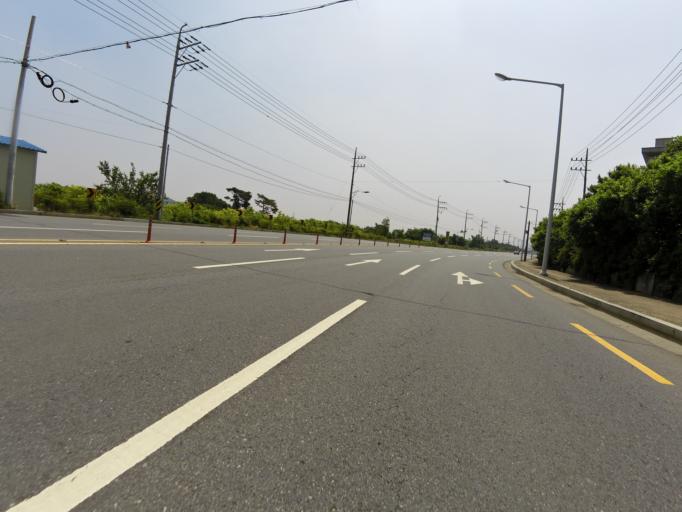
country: KR
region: Gyeongsangbuk-do
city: Gyeongsan-si
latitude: 35.8517
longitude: 128.7272
